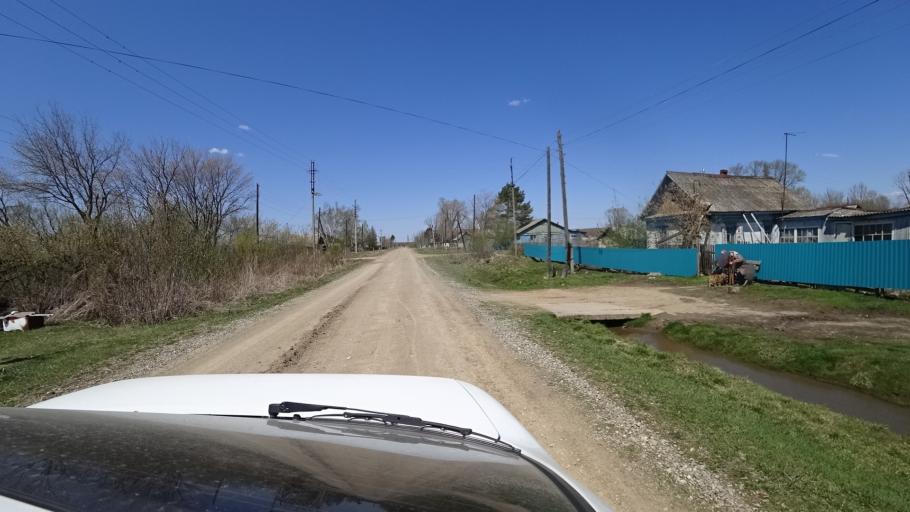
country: RU
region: Primorskiy
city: Lazo
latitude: 45.7983
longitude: 133.7641
